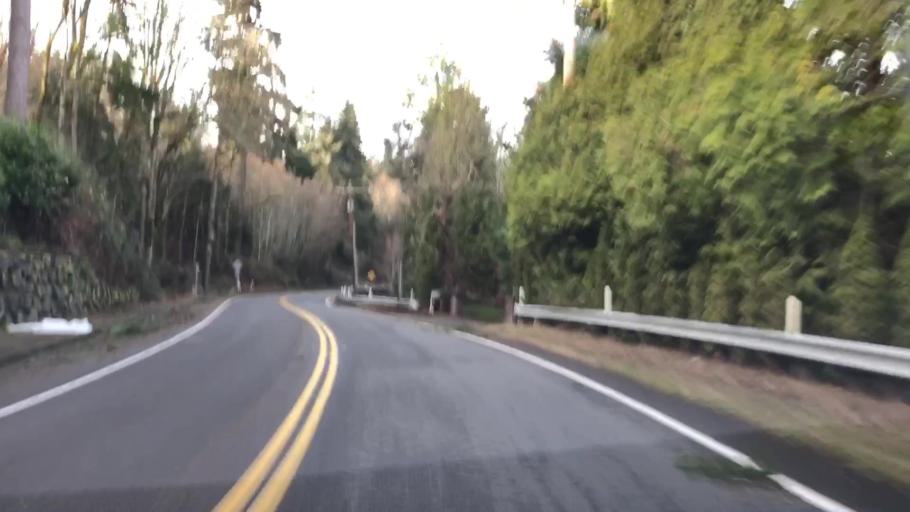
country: US
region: Washington
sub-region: King County
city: West Lake Sammamish
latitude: 47.5669
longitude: -122.1222
